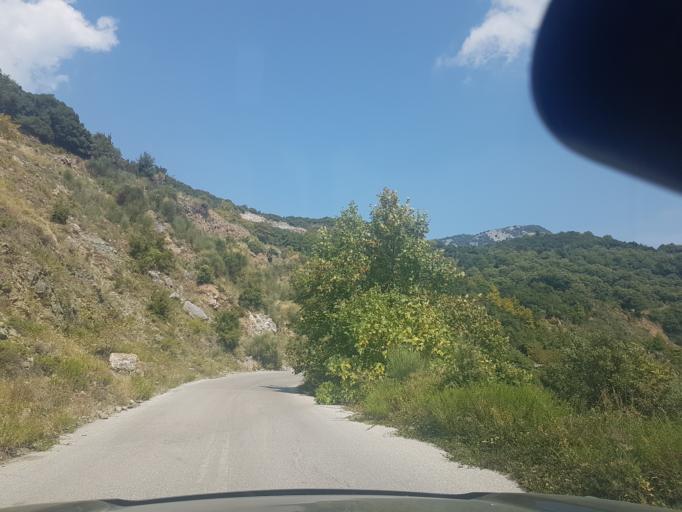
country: GR
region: Central Greece
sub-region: Nomos Evvoias
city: Yimnon
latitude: 38.6420
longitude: 23.8959
